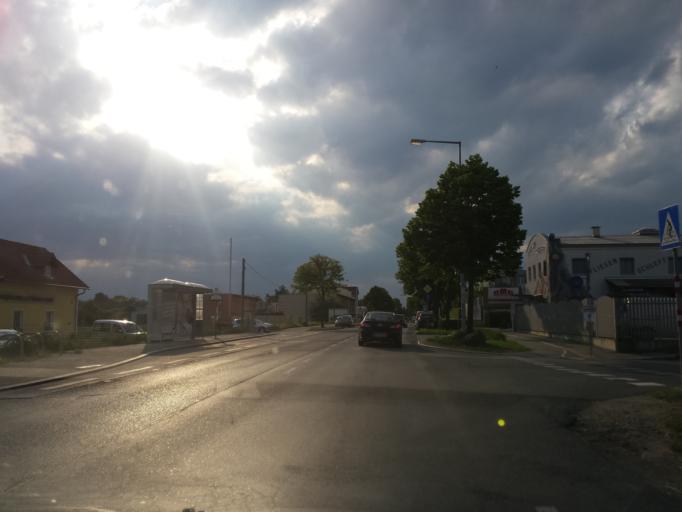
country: AT
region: Lower Austria
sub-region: Politischer Bezirk Ganserndorf
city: Gross-Enzersdorf
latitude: 48.2081
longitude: 16.5409
